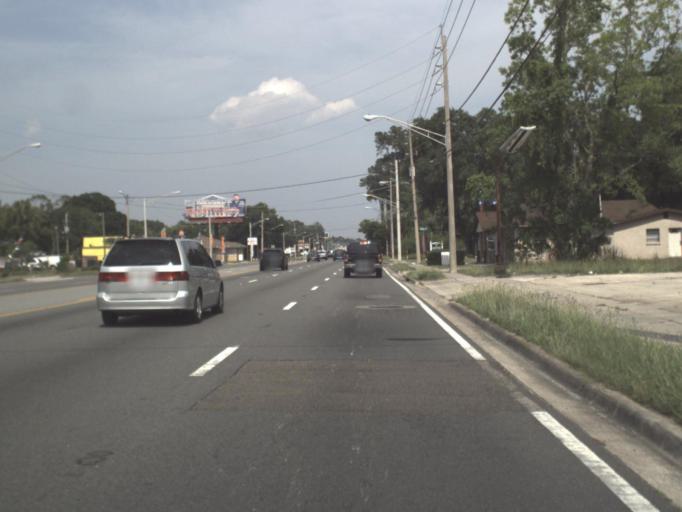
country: US
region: Florida
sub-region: Clay County
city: Bellair-Meadowbrook Terrace
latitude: 30.2483
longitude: -81.7520
